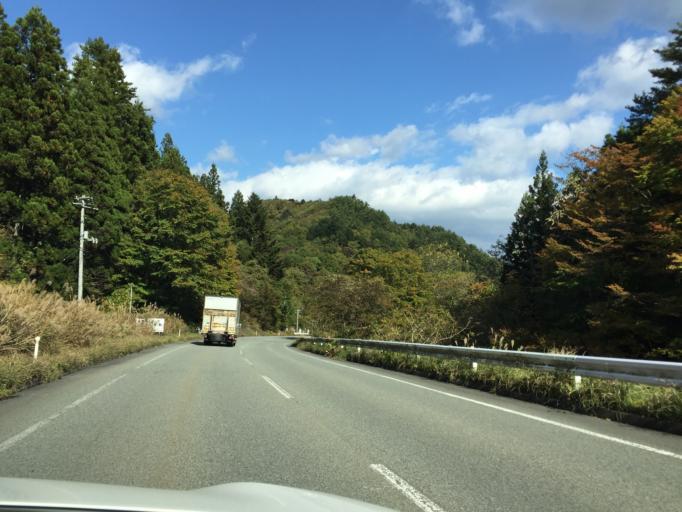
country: JP
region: Fukushima
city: Namie
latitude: 37.3461
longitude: 140.8712
